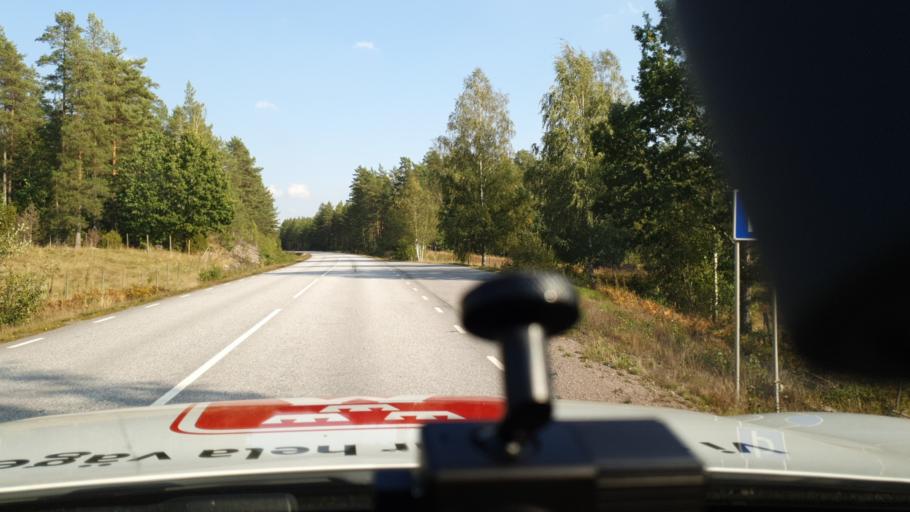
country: SE
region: Kalmar
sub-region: Vimmerby Kommun
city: Vimmerby
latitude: 57.5956
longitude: 16.0401
